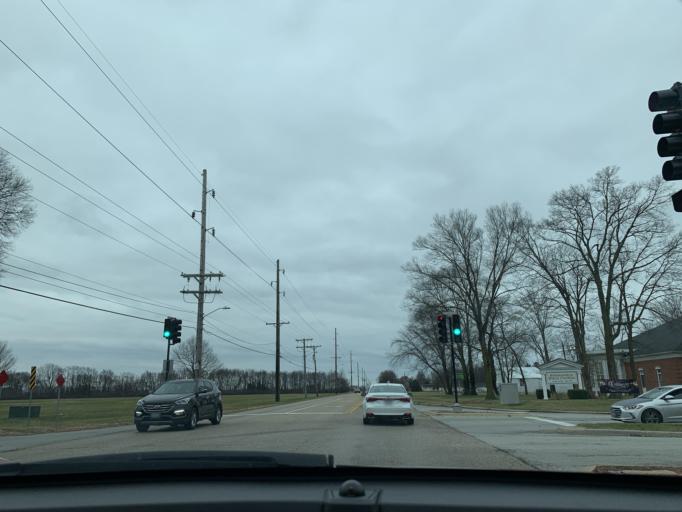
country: US
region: Illinois
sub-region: Sangamon County
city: Jerome
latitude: 39.7571
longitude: -89.6868
